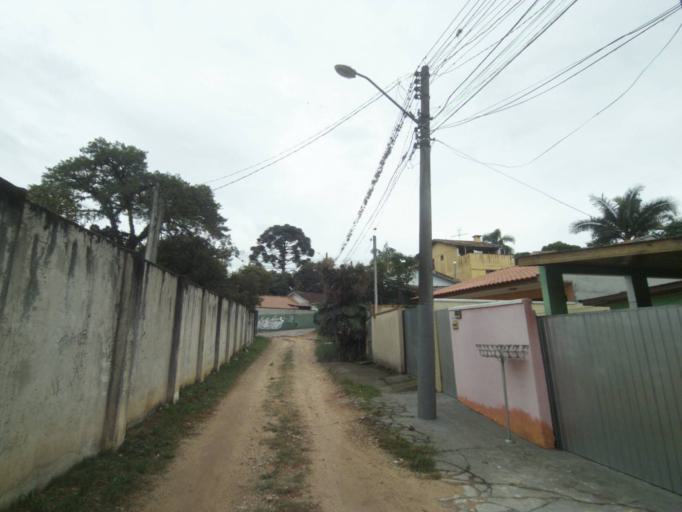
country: BR
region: Parana
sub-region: Curitiba
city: Curitiba
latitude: -25.4530
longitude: -49.3133
